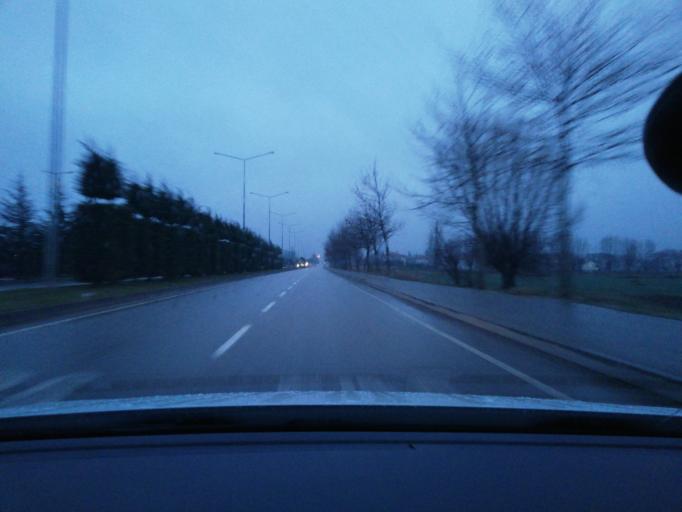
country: TR
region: Bolu
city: Bolu
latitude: 40.7174
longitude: 31.6143
